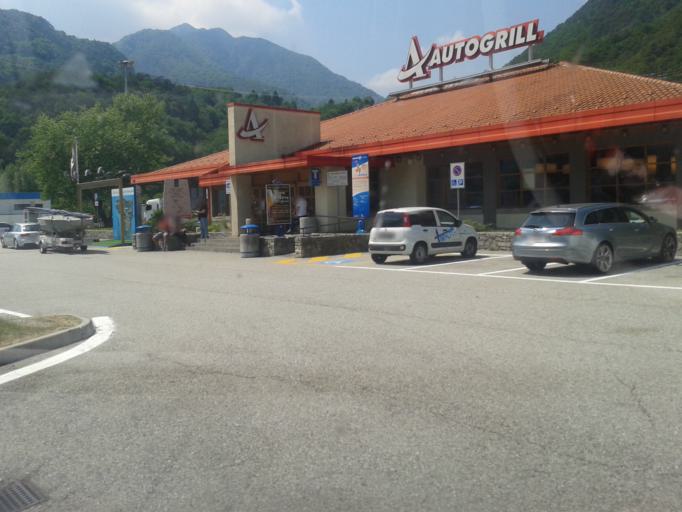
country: IT
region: Friuli Venezia Giulia
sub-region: Provincia di Udine
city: Moggio di Sotto
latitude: 46.3987
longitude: 13.1685
